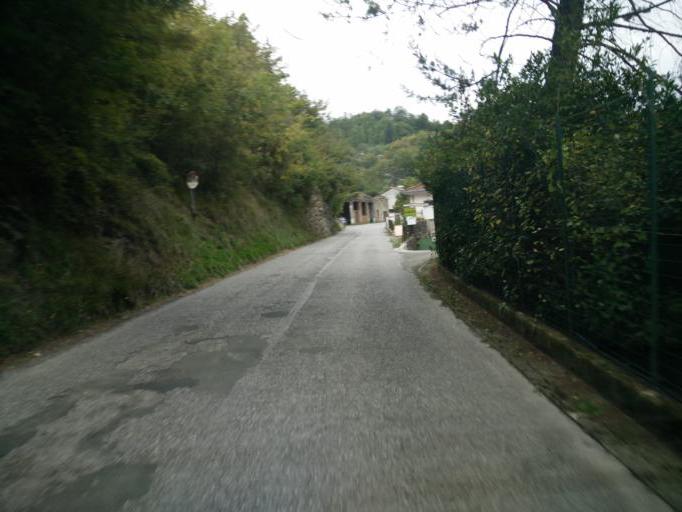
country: IT
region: Tuscany
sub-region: Provincia di Massa-Carrara
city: Fivizzano
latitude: 44.1983
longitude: 10.1223
